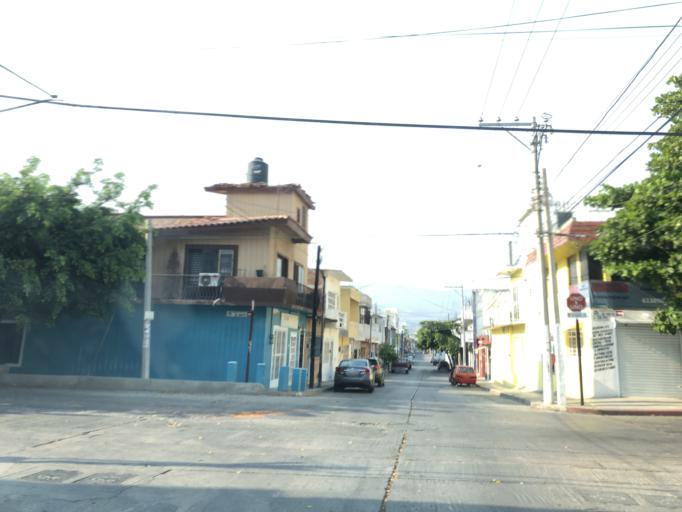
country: MX
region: Chiapas
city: Tuxtla Gutierrez
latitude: 16.7492
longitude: -93.1222
